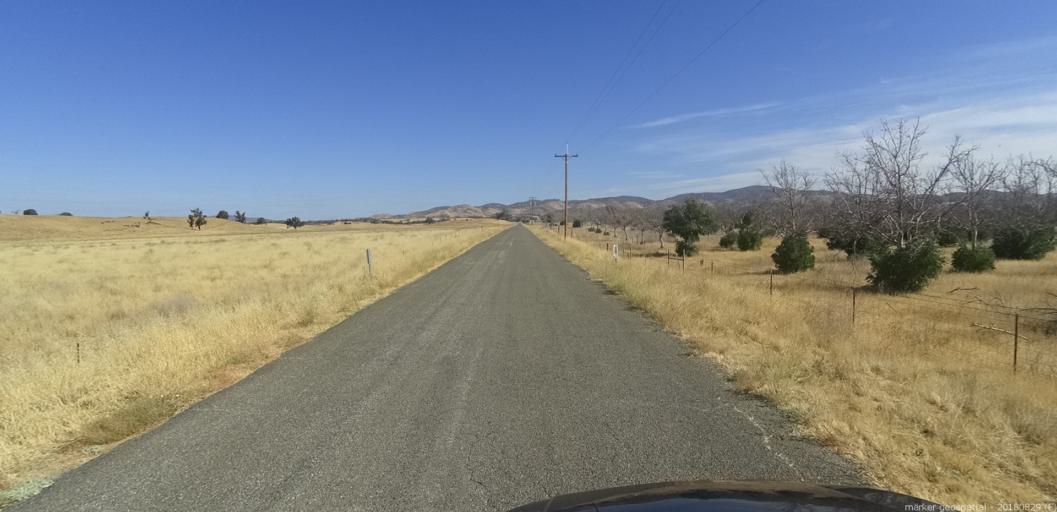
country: US
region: California
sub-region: Monterey County
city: King City
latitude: 35.9523
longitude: -121.1176
